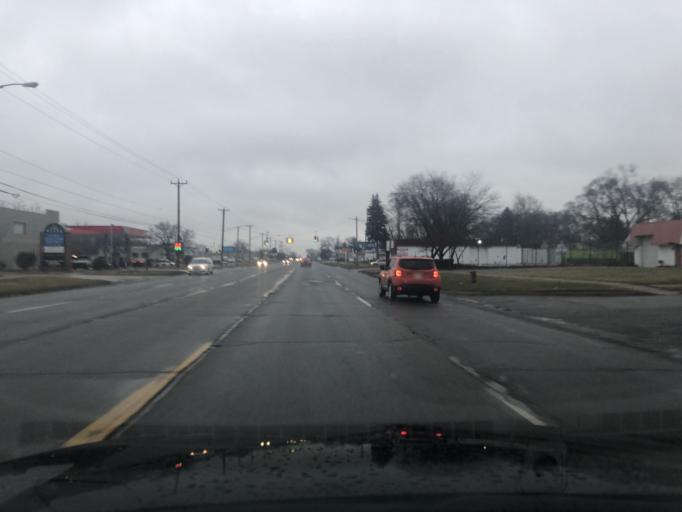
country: US
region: Michigan
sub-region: Wayne County
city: Taylor
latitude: 42.2687
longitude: -83.2863
